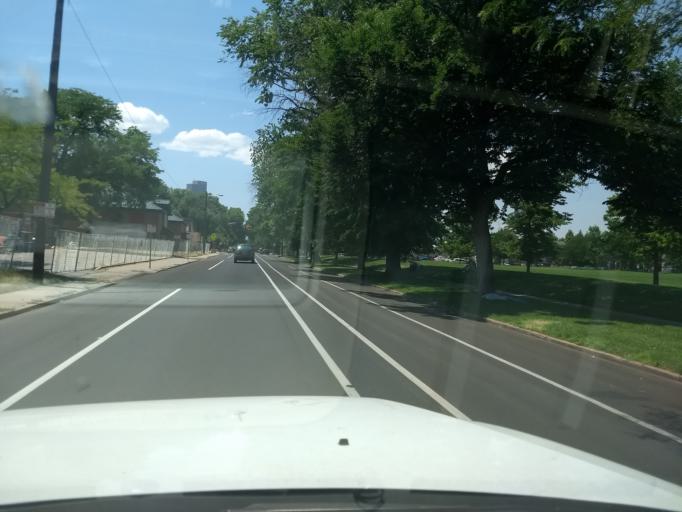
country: US
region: Colorado
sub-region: Denver County
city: Denver
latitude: 39.7603
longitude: -104.9761
